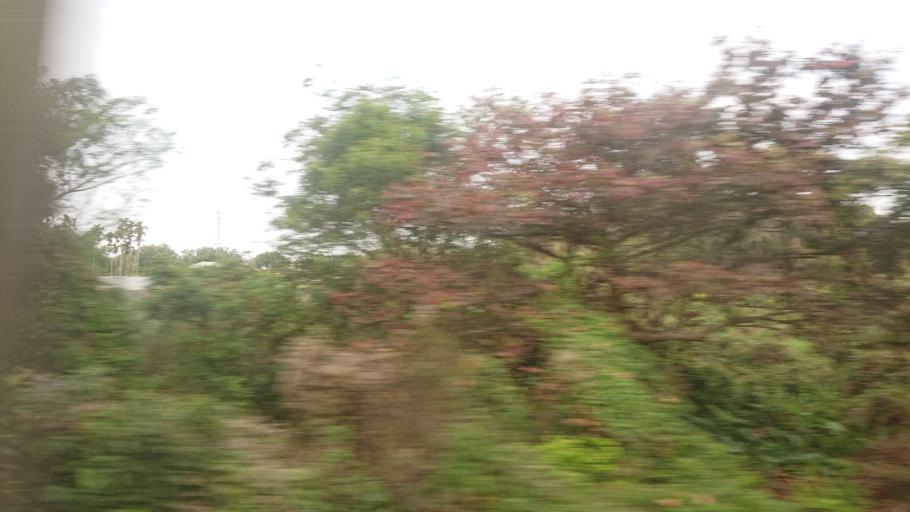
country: TW
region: Taiwan
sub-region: Yunlin
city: Douliu
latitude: 23.7659
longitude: 120.6227
